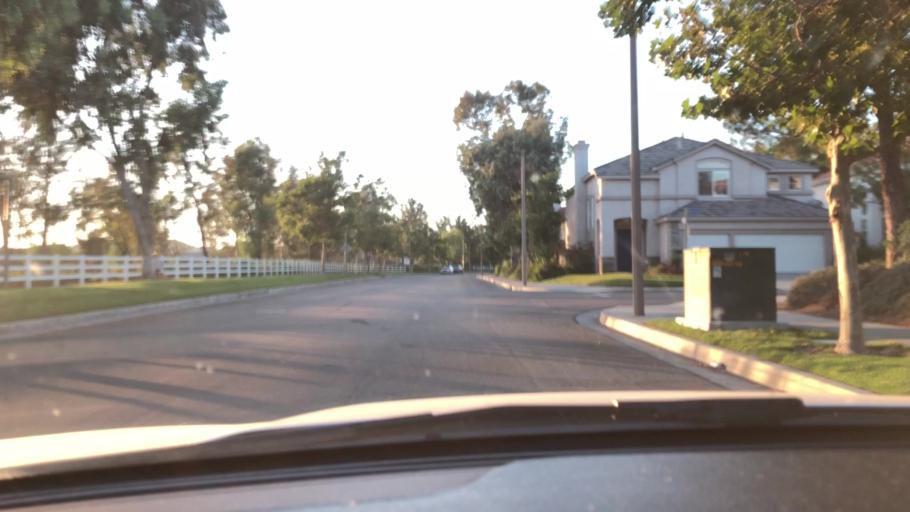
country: US
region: California
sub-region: Los Angeles County
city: Santa Clarita
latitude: 34.4552
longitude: -118.5443
